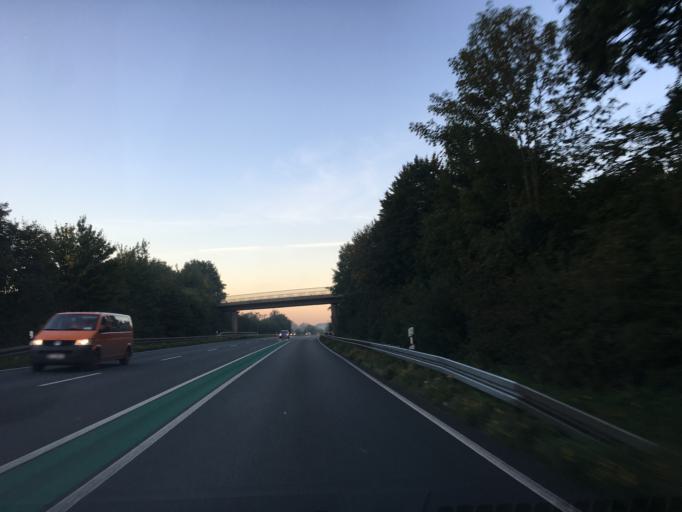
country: DE
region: North Rhine-Westphalia
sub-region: Regierungsbezirk Munster
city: Laer
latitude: 52.1070
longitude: 7.3806
